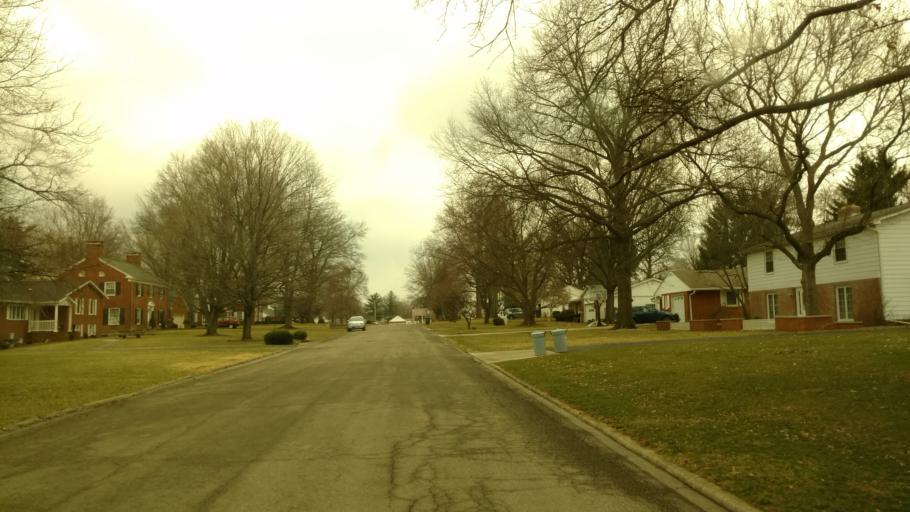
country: US
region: Ohio
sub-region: Richland County
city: Shelby
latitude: 40.8760
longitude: -82.6474
